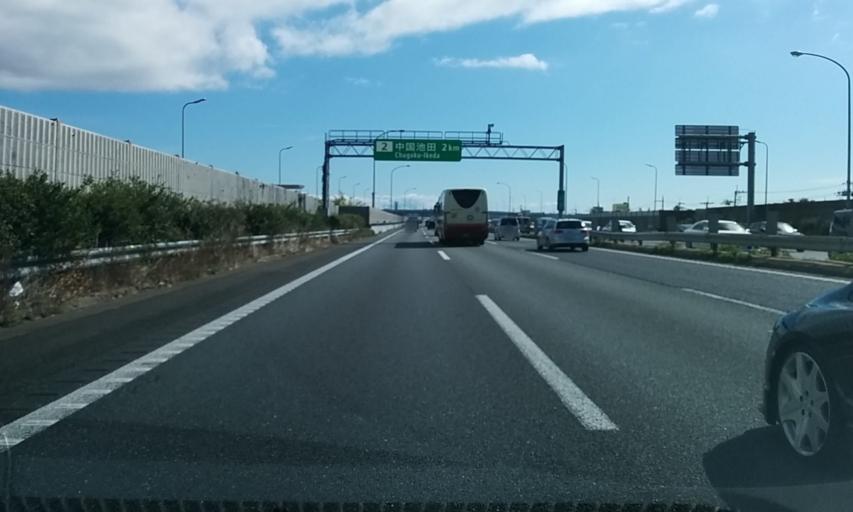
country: JP
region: Hyogo
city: Kawanishi
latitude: 34.8112
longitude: 135.4093
